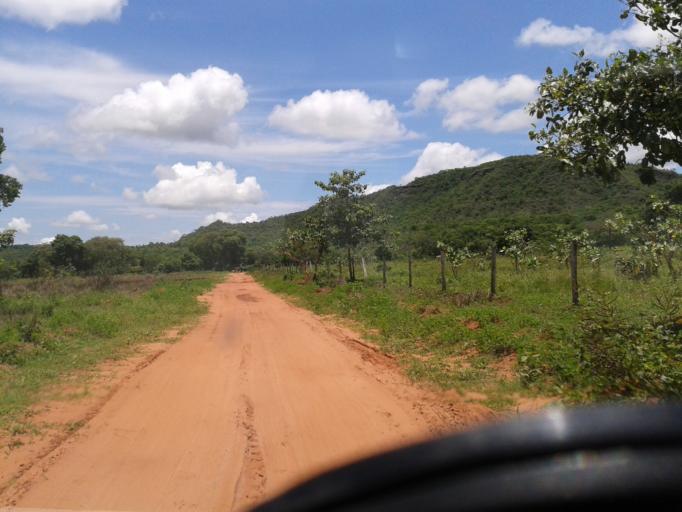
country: BR
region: Minas Gerais
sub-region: Santa Vitoria
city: Santa Vitoria
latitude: -18.9894
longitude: -49.9024
